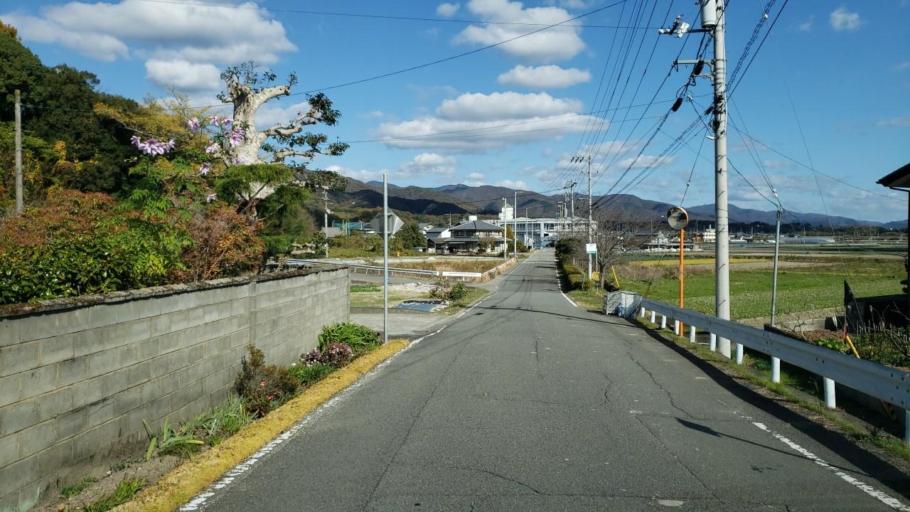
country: JP
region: Tokushima
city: Wakimachi
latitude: 34.0736
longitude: 134.1921
